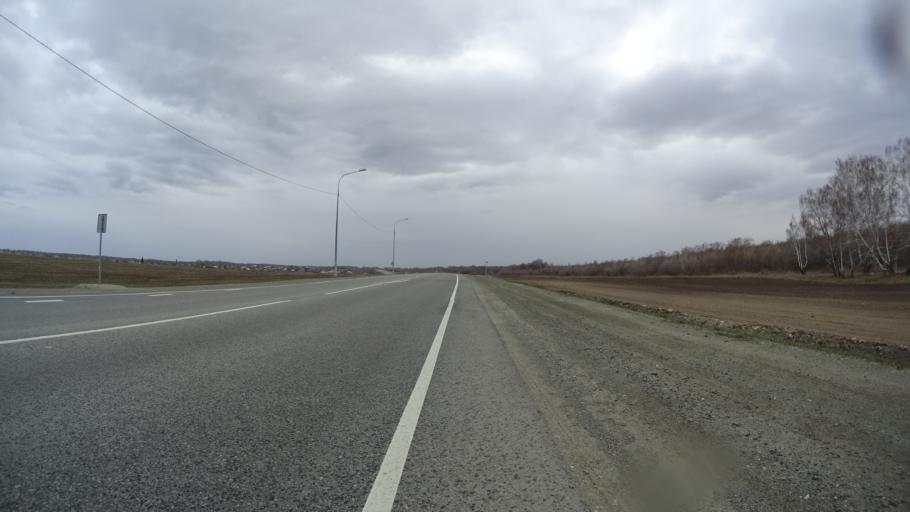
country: RU
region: Chelyabinsk
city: Krasnogorskiy
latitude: 54.6814
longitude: 61.2469
